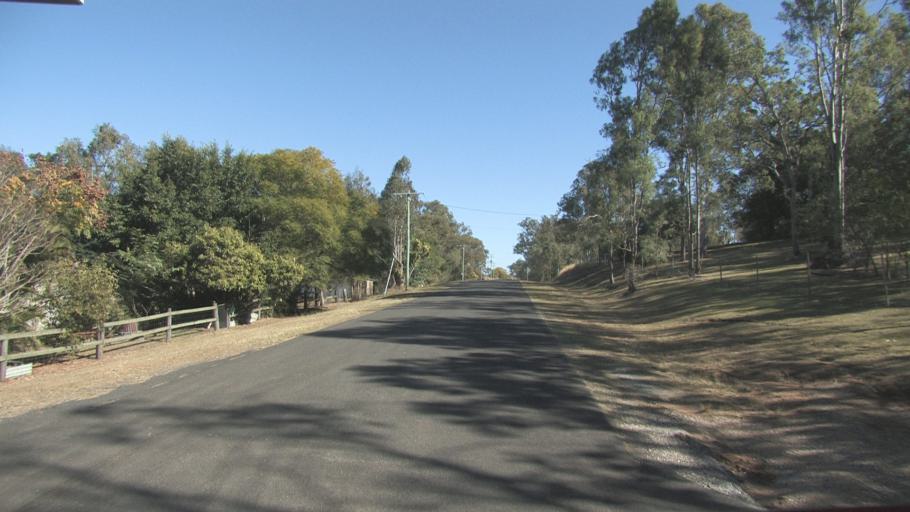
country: AU
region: Queensland
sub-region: Logan
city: Cedar Vale
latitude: -27.8930
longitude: 152.9814
